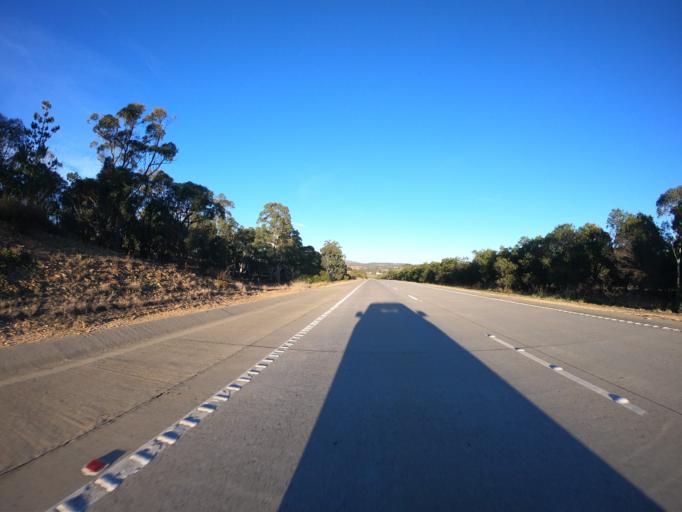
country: AU
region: New South Wales
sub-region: Yass Valley
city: Gundaroo
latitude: -35.1145
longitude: 149.3594
